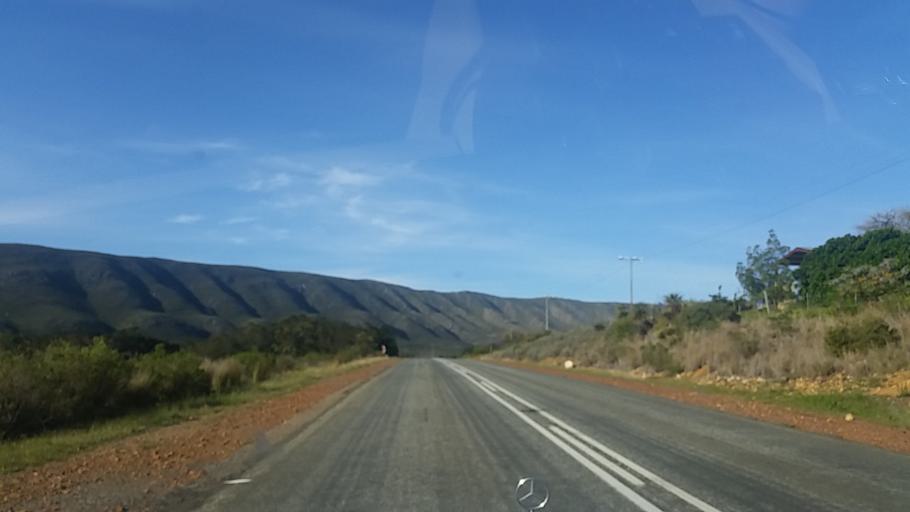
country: ZA
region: Western Cape
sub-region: Eden District Municipality
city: Knysna
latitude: -33.7730
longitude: 22.9594
